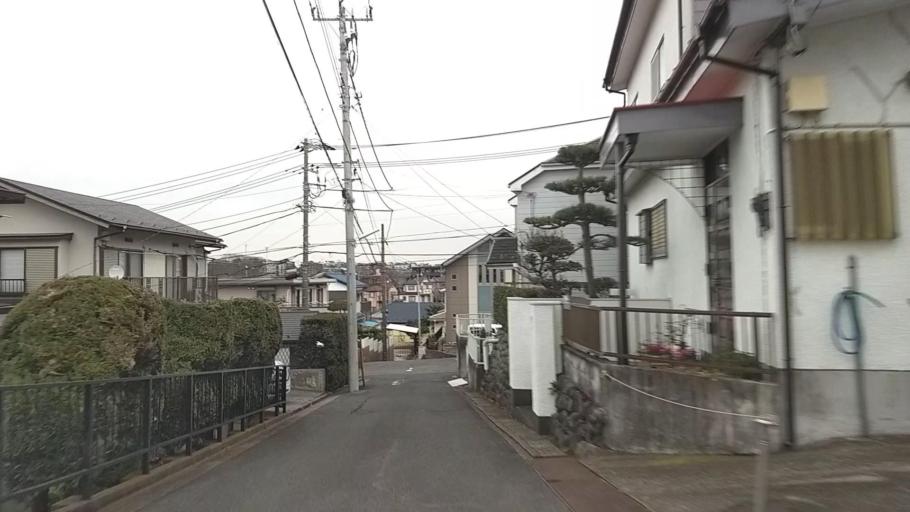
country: JP
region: Tokyo
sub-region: Machida-shi
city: Machida
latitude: 35.5605
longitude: 139.4450
